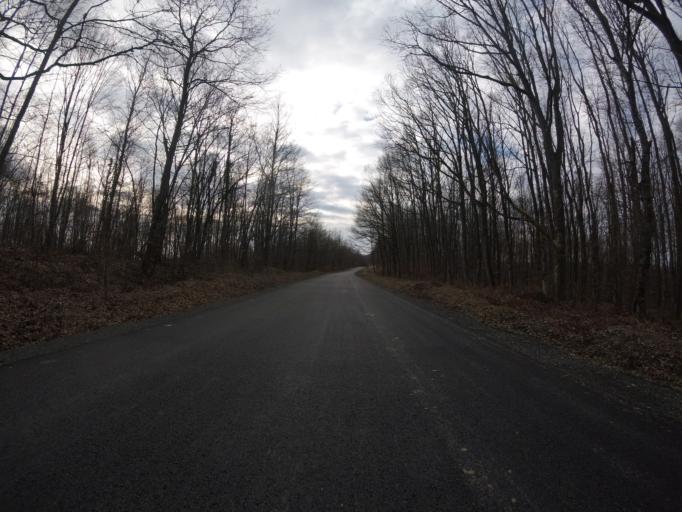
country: HR
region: Sisacko-Moslavacka
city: Glina
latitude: 45.4941
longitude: 16.0459
